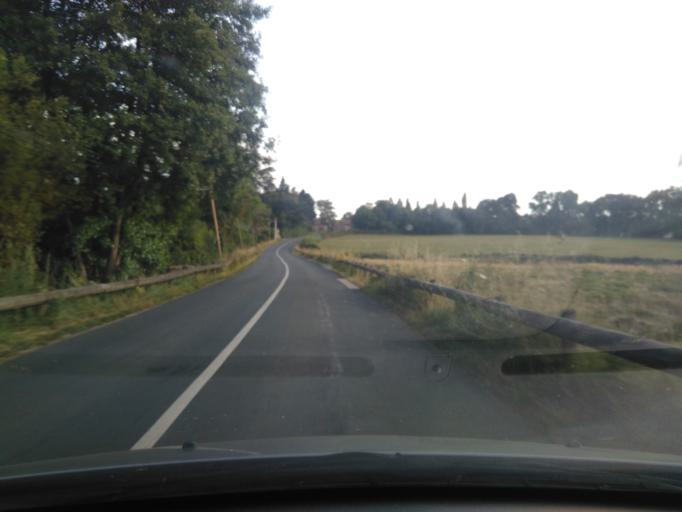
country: FR
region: Pays de la Loire
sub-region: Departement de la Vendee
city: Nesmy
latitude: 46.5971
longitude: -1.4045
